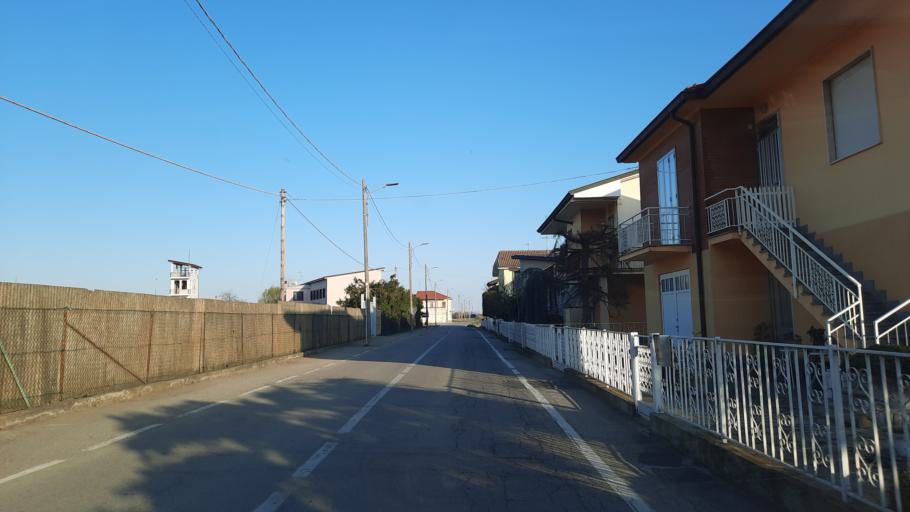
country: IT
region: Piedmont
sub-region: Provincia di Vercelli
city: Trino
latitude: 45.2016
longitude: 8.2995
